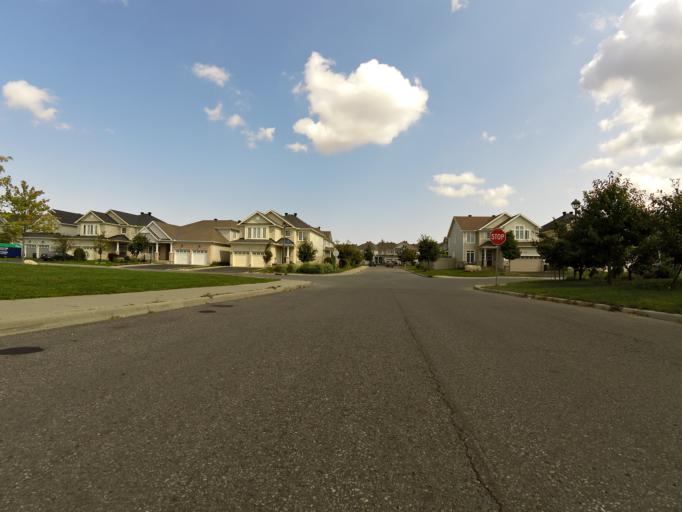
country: CA
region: Ontario
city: Bells Corners
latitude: 45.2559
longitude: -75.7326
